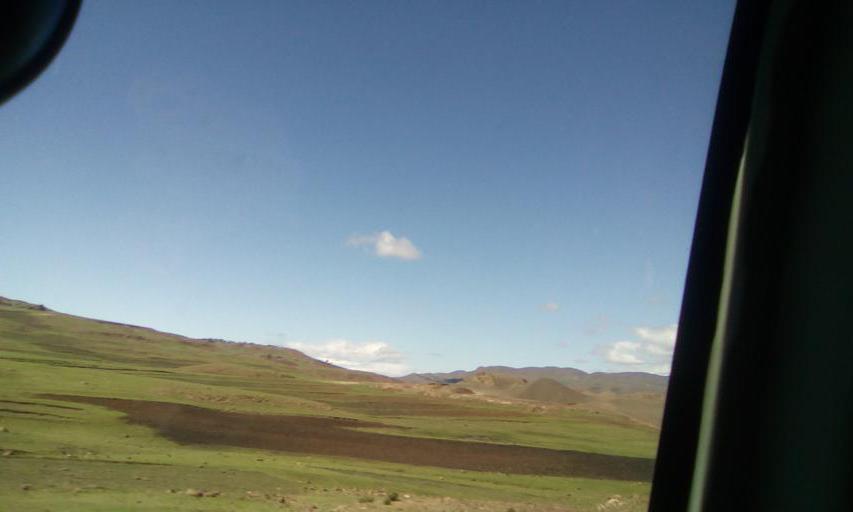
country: LS
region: Maseru
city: Nako
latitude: -29.8862
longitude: 28.0964
